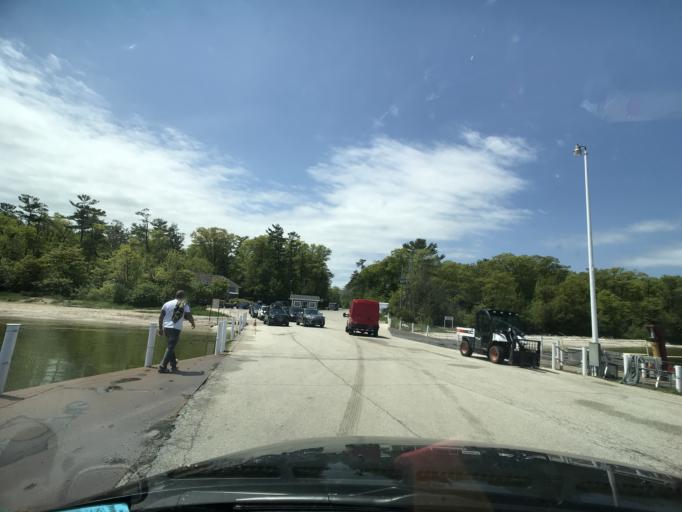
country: US
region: Michigan
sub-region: Delta County
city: Escanaba
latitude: 45.2907
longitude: -86.9770
